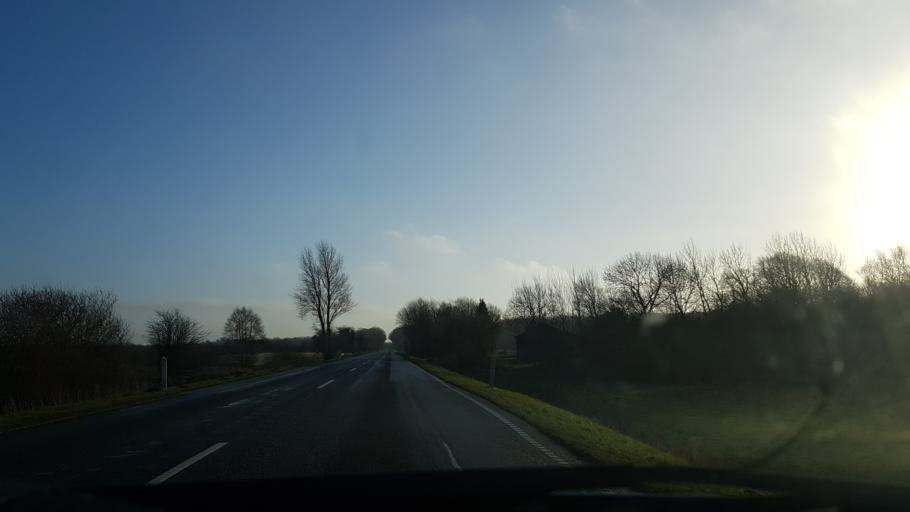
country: DK
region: South Denmark
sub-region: Tonder Kommune
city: Toftlund
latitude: 55.2277
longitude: 9.1722
